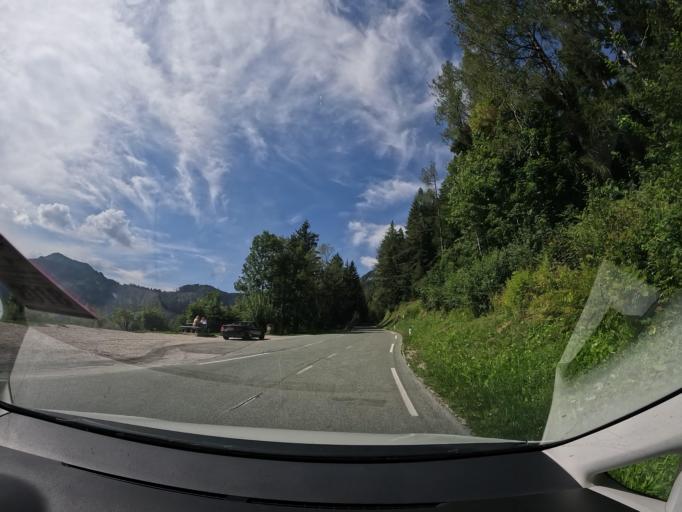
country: AT
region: Carinthia
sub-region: Politischer Bezirk Feldkirchen
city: Glanegg
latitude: 46.7389
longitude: 14.2098
